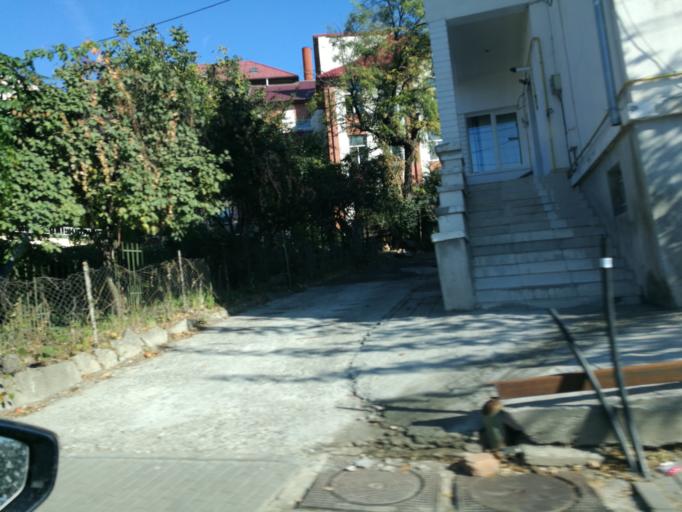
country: RO
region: Iasi
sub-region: Municipiul Iasi
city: Iasi
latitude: 47.1703
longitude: 27.5739
